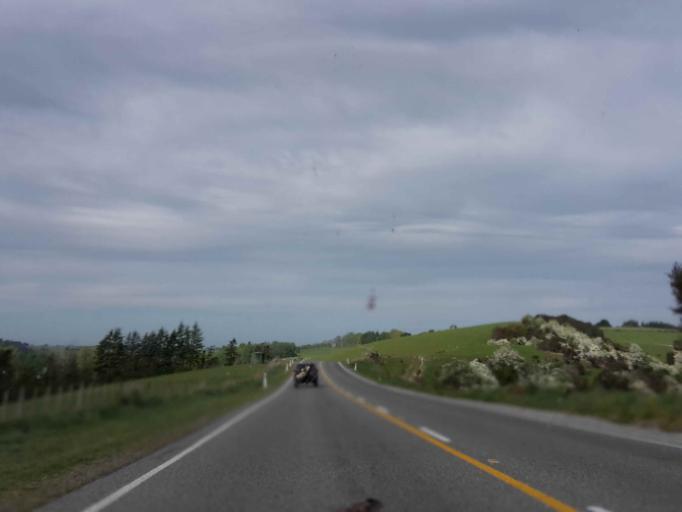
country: NZ
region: Canterbury
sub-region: Timaru District
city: Pleasant Point
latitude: -44.1198
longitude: 171.1200
